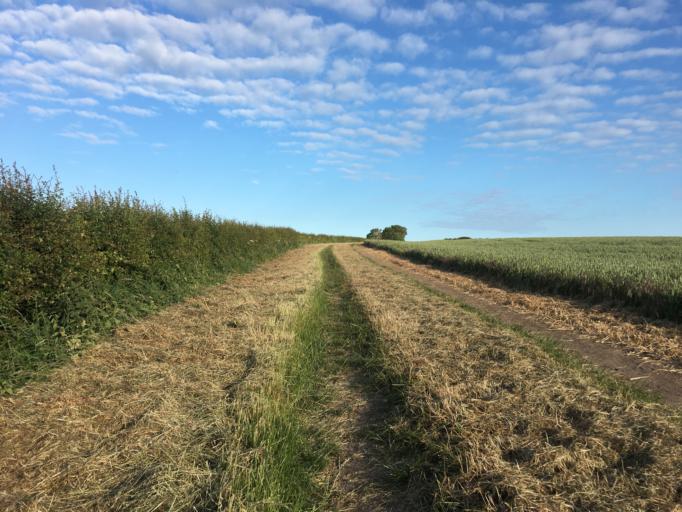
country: GB
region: England
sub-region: Northumberland
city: Bamburgh
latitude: 55.6015
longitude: -1.6993
